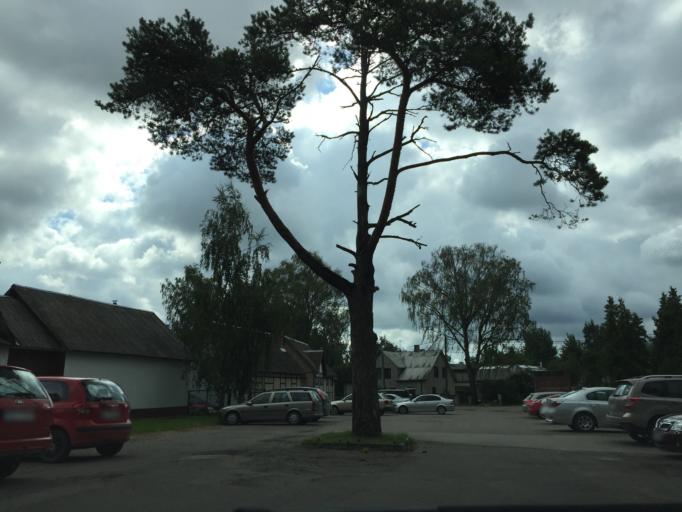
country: LV
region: Sigulda
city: Sigulda
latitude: 57.1530
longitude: 24.8580
